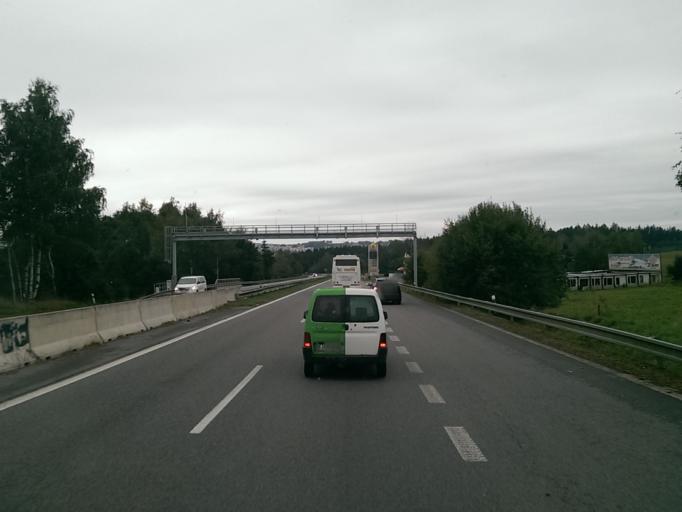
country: CZ
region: Vysocina
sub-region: Okres Jihlava
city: Jihlava
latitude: 49.4223
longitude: 15.5850
